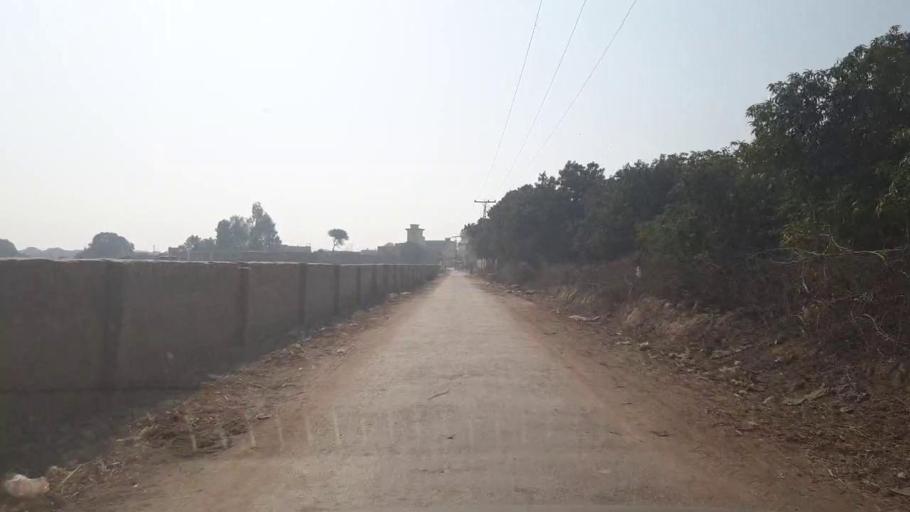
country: PK
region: Sindh
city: Tando Allahyar
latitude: 25.4753
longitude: 68.7730
